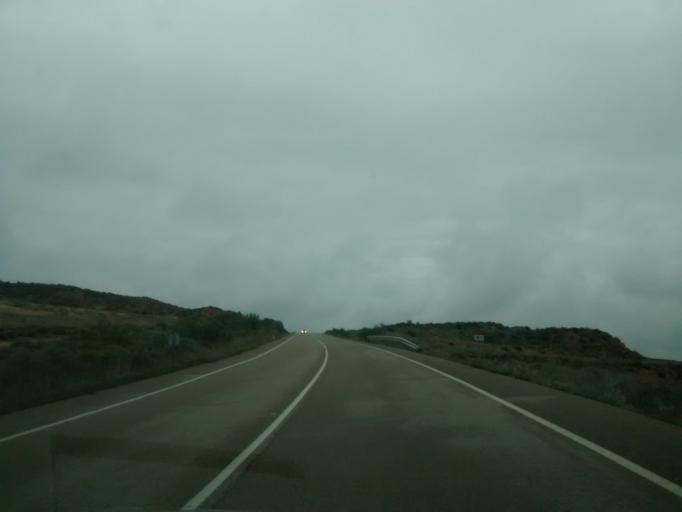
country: ES
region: Aragon
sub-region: Provincia de Zaragoza
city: Caspe
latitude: 41.2078
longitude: 0.0148
